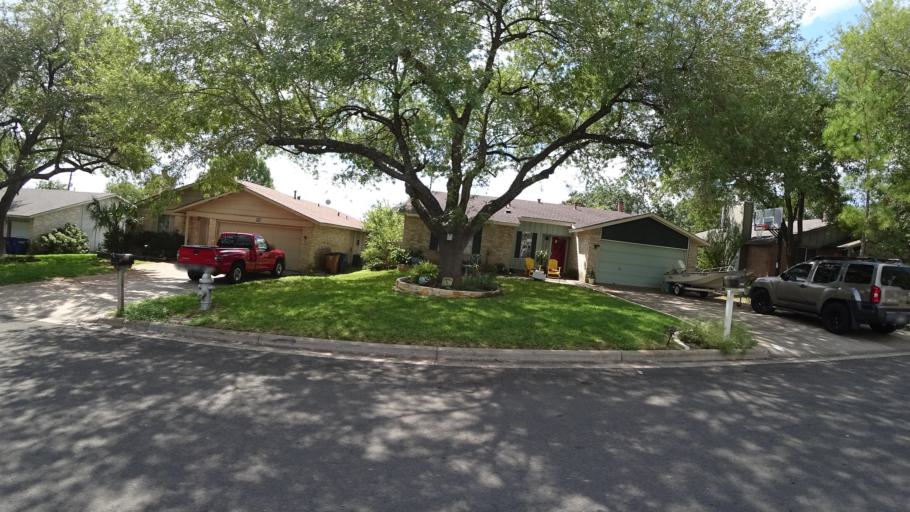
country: US
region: Texas
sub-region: Travis County
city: Onion Creek
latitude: 30.1898
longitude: -97.7820
